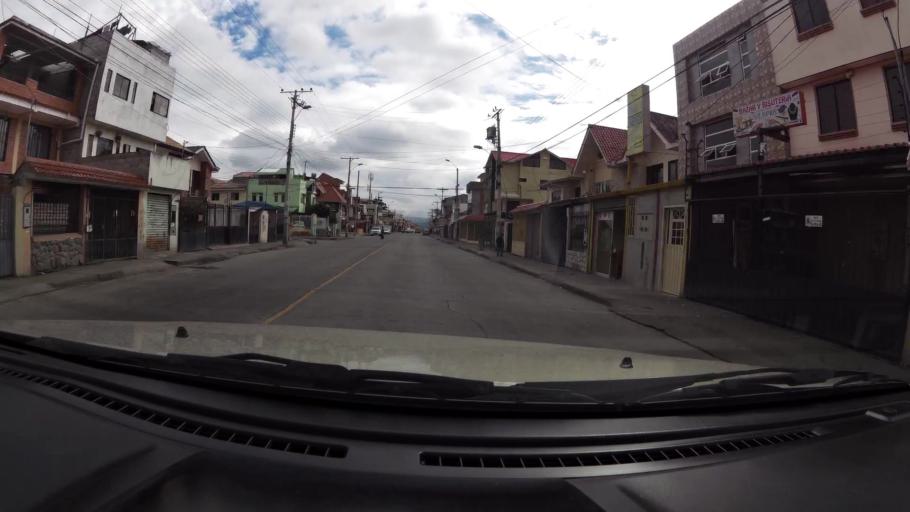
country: EC
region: Azuay
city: Cuenca
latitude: -2.8947
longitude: -78.9803
